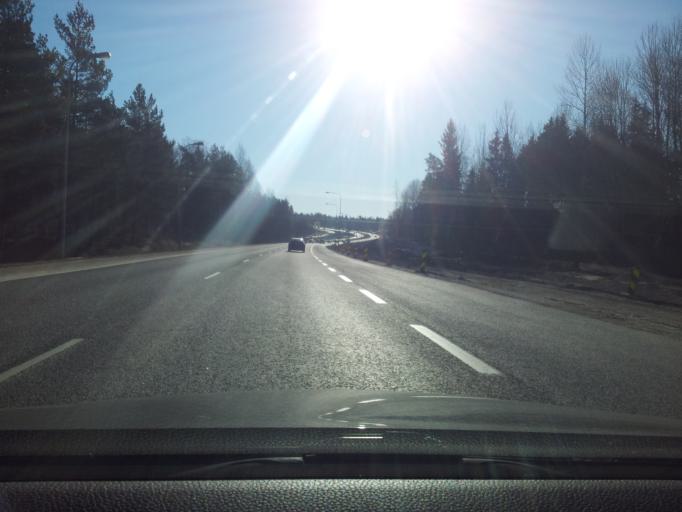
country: FI
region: Uusimaa
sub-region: Helsinki
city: Vantaa
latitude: 60.2351
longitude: 25.0453
